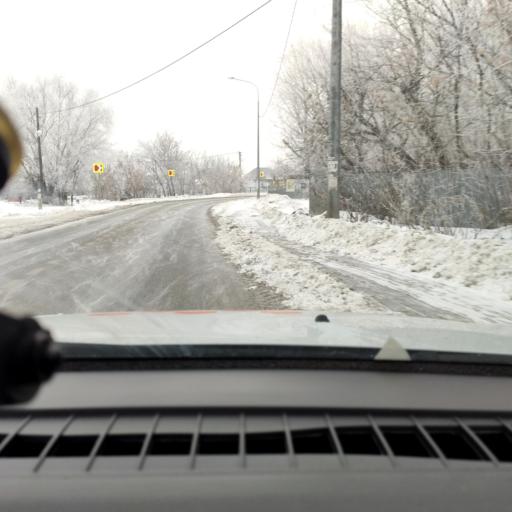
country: RU
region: Samara
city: Dubovyy Umet
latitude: 53.0767
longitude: 50.2168
